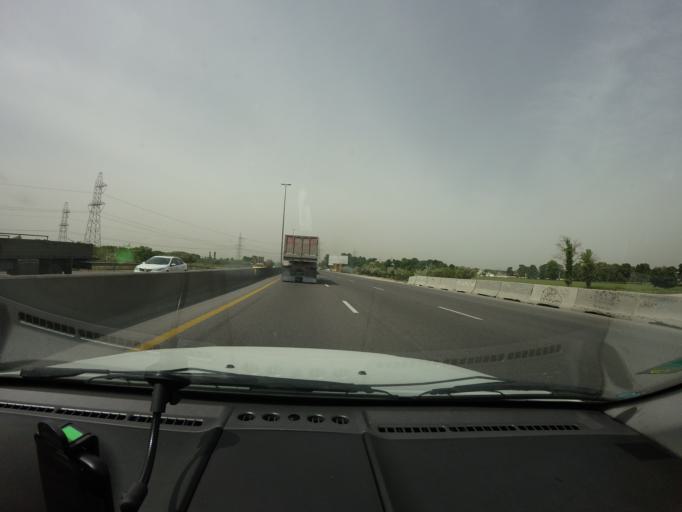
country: IR
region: Tehran
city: Eslamshahr
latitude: 35.6207
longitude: 51.2249
